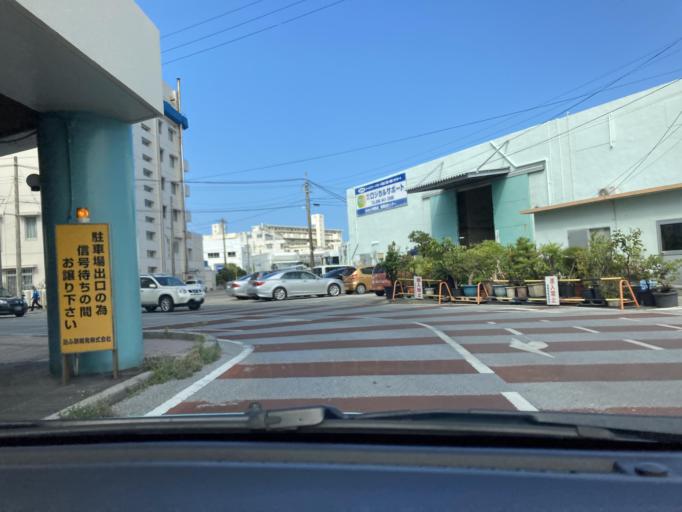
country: JP
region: Okinawa
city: Naha-shi
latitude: 26.2239
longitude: 127.6821
